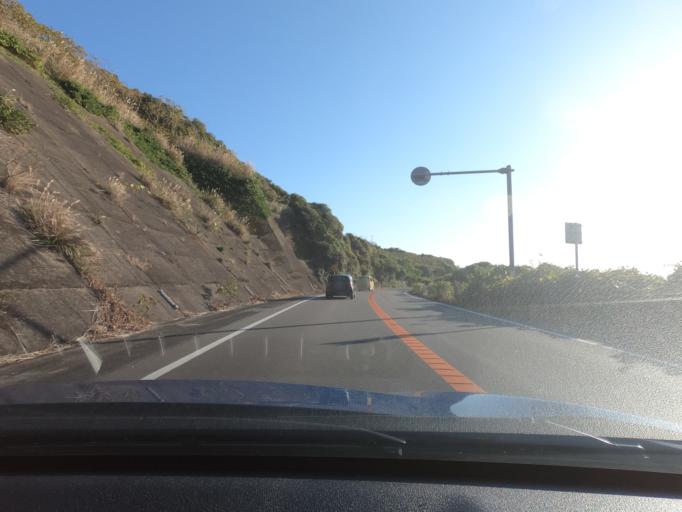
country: JP
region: Kagoshima
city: Akune
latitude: 31.9530
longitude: 130.2165
